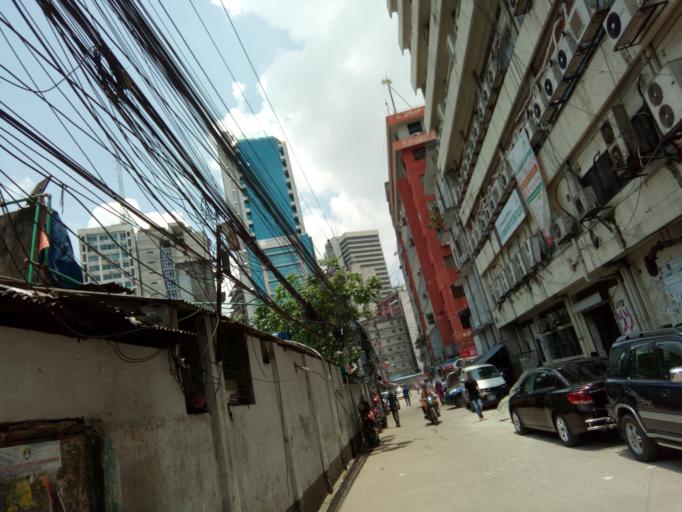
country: BD
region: Dhaka
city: Paltan
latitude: 23.7281
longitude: 90.4199
